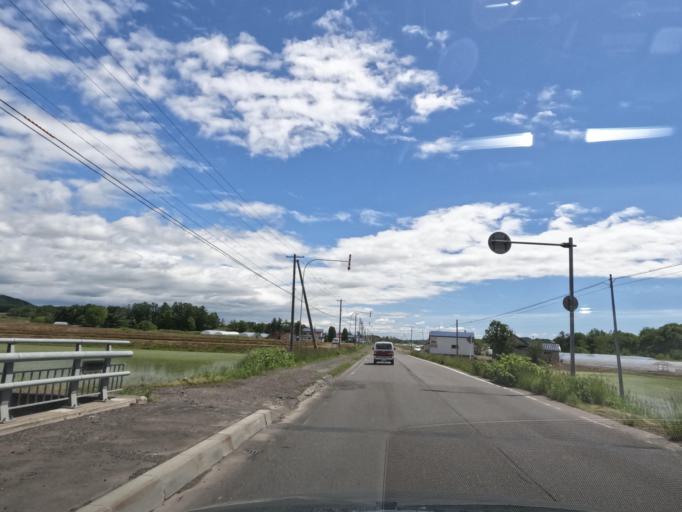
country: JP
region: Hokkaido
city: Iwamizawa
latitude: 43.1425
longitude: 141.8054
